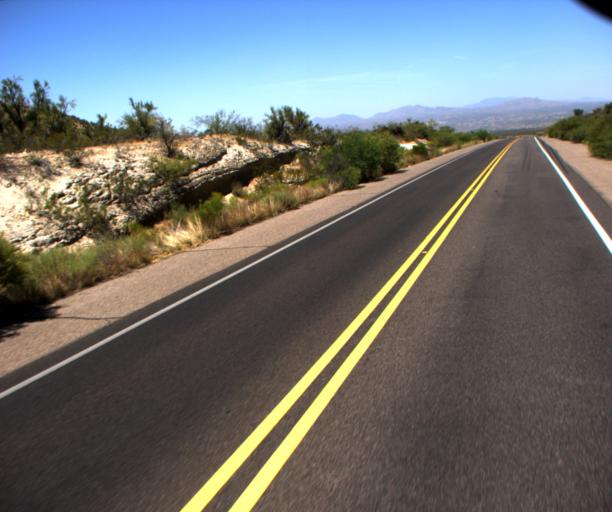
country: US
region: Arizona
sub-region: Gila County
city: Peridot
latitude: 33.2865
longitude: -110.3748
